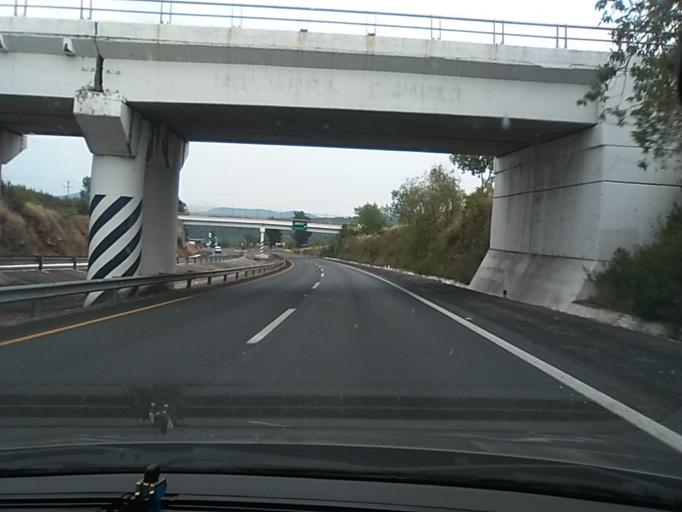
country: MX
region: Michoacan
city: Panindicuaro de la Reforma
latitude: 19.9715
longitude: -101.7621
